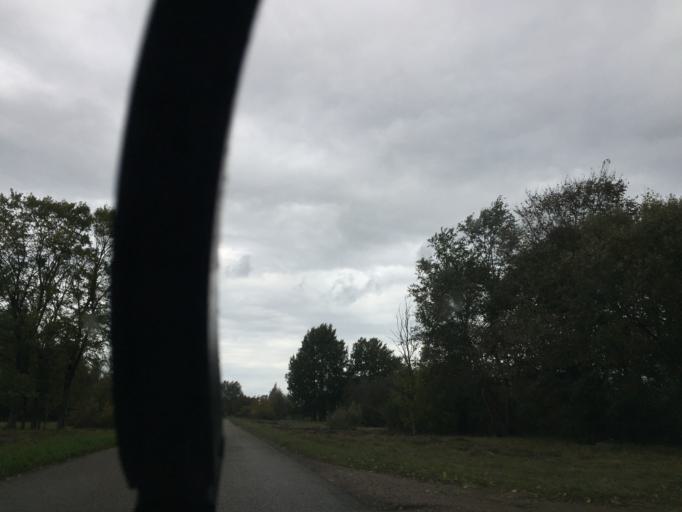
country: LV
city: Tireli
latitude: 56.7887
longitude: 23.6290
